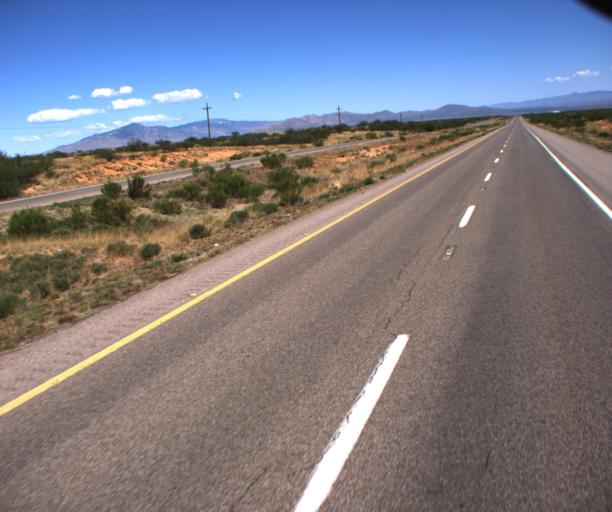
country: US
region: Arizona
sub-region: Cochise County
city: Whetstone
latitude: 31.8955
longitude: -110.3410
